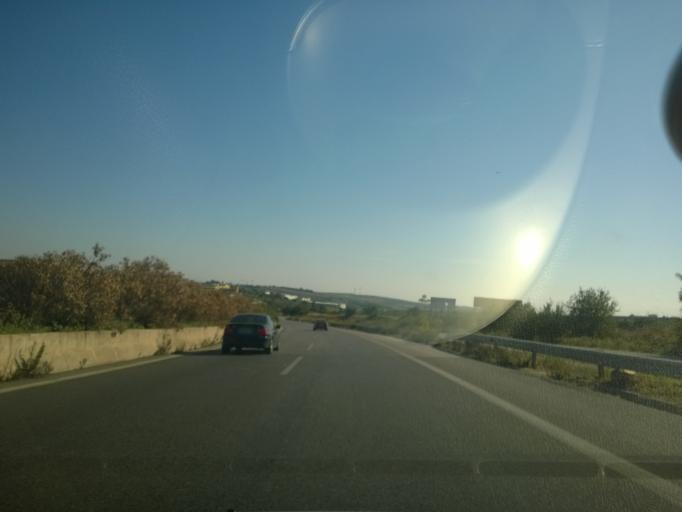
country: GR
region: Central Macedonia
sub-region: Nomos Thessalonikis
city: Mesimeri
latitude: 40.4124
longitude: 23.0235
